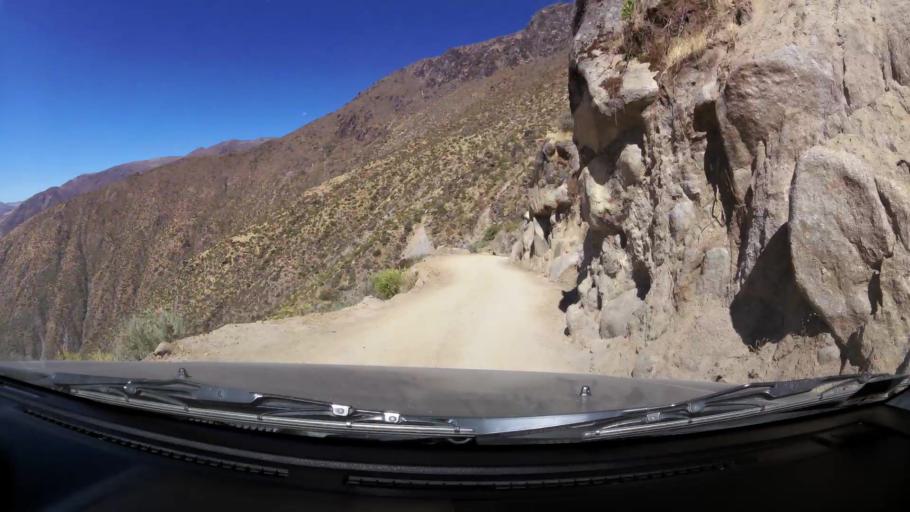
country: PE
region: Huancavelica
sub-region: Huaytara
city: Quito-Arma
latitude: -13.6192
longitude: -75.3513
